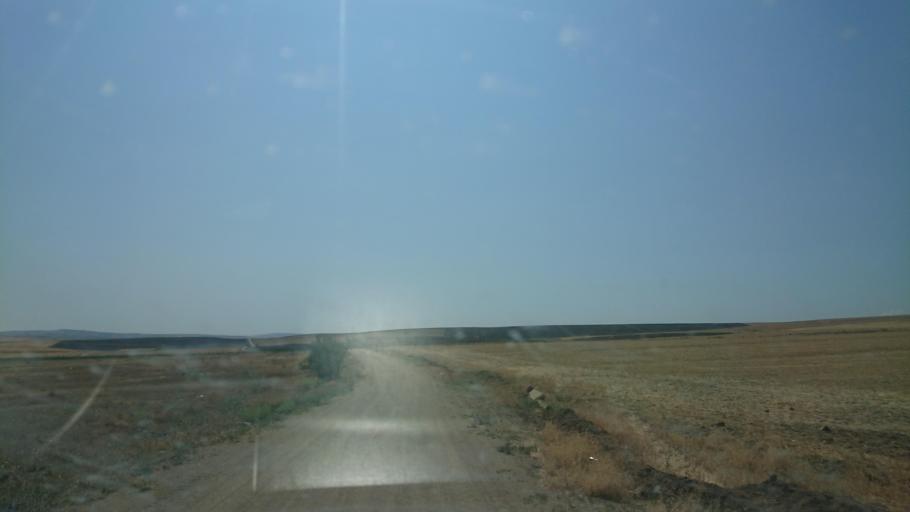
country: TR
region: Aksaray
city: Sariyahsi
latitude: 38.9571
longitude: 33.9126
